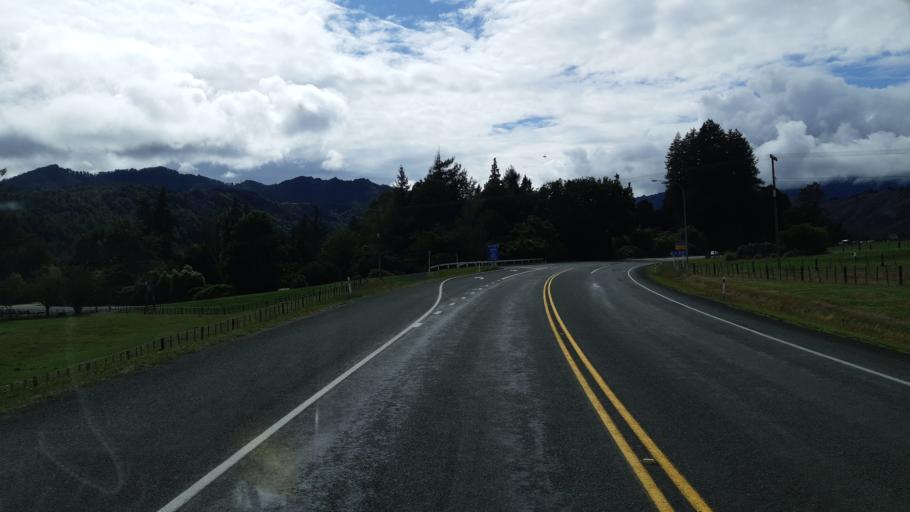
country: NZ
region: West Coast
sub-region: Buller District
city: Westport
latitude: -41.7969
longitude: 172.3393
